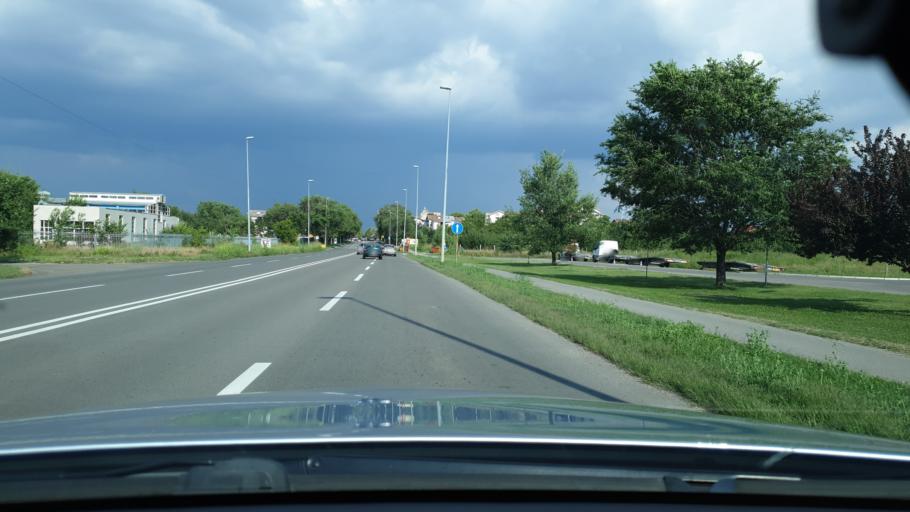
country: RS
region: Autonomna Pokrajina Vojvodina
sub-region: Srednjebanatski Okrug
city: Zrenjanin
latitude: 45.3800
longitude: 20.3555
